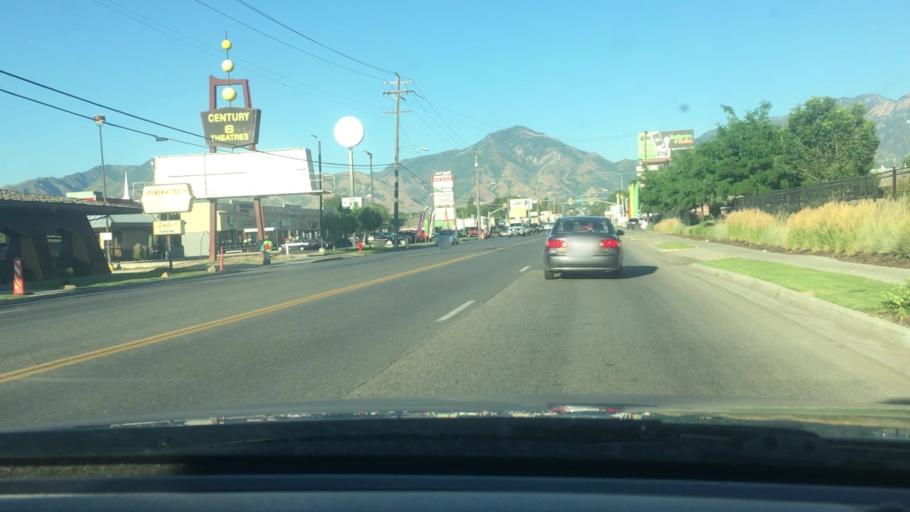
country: US
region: Utah
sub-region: Salt Lake County
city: Centerfield
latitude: 40.6998
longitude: -111.8850
